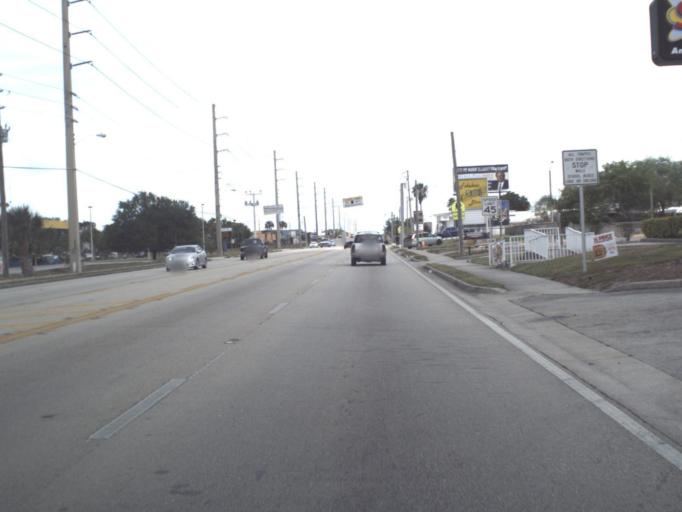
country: US
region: Florida
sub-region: Brevard County
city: Cocoa
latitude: 28.3738
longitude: -80.7550
